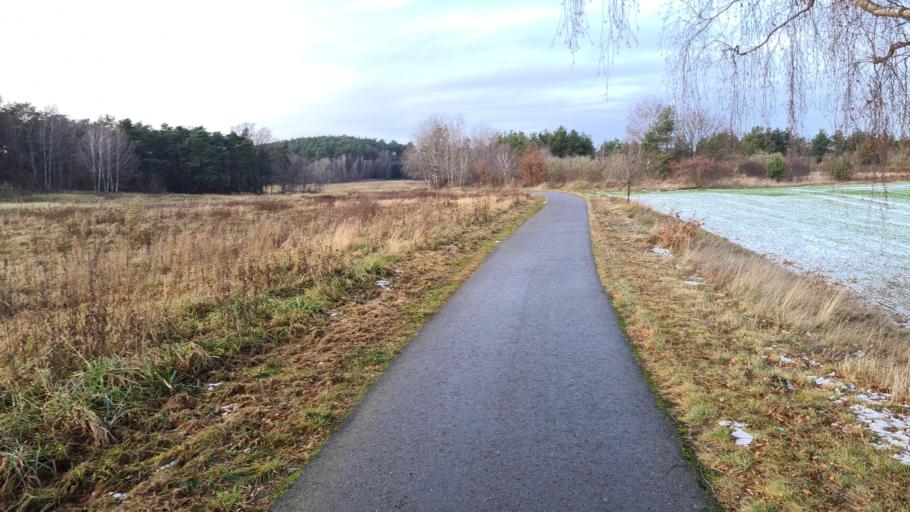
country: DE
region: Brandenburg
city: Groden
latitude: 51.3958
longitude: 13.5858
